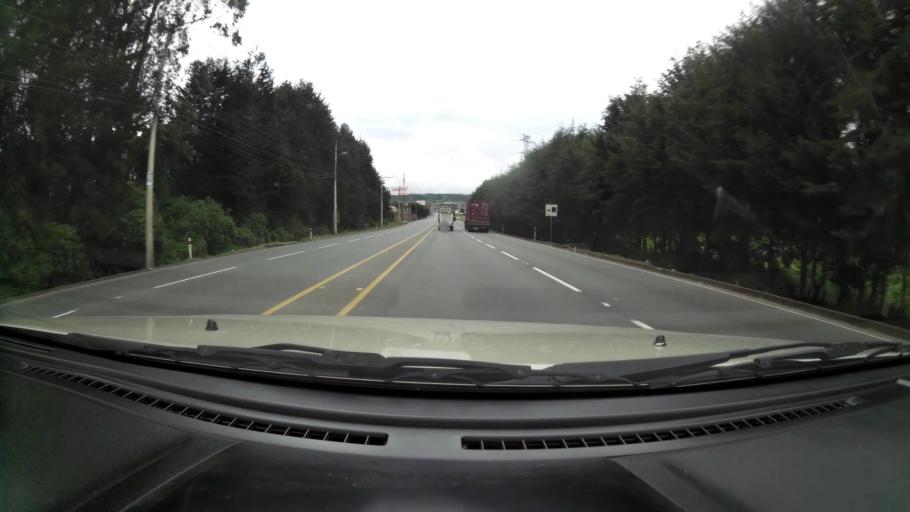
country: EC
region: Pichincha
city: Machachi
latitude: -0.4420
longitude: -78.6083
